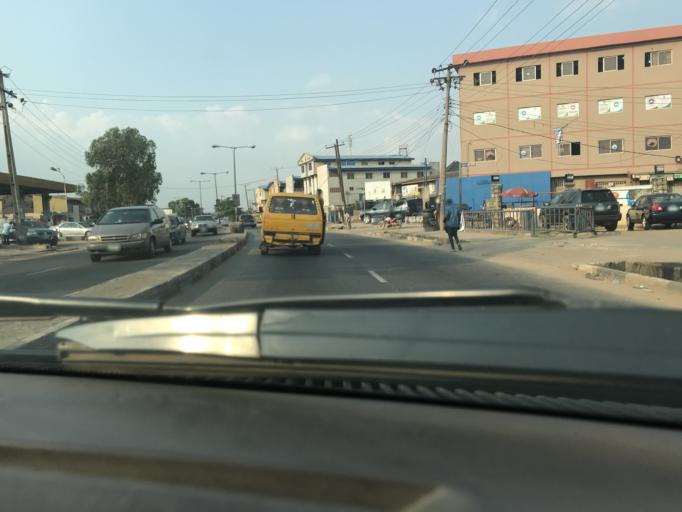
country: NG
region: Lagos
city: Agege
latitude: 6.5907
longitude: 3.2879
